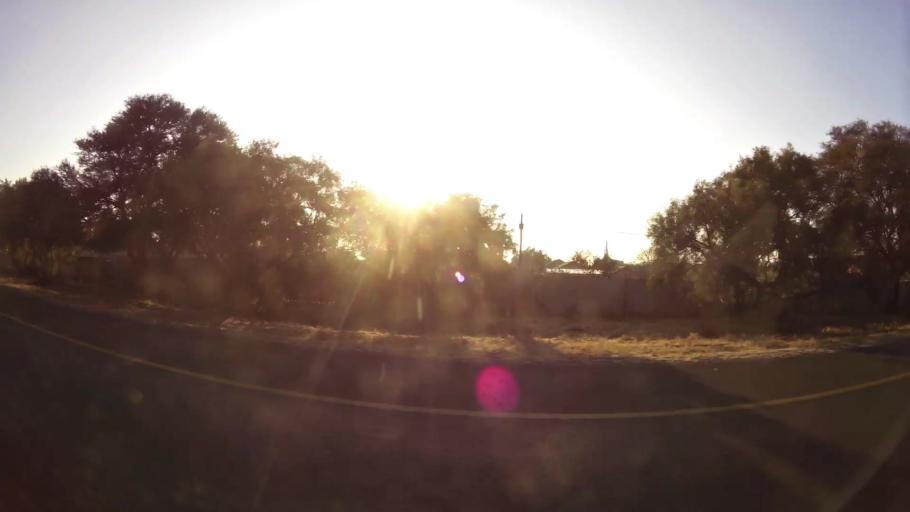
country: ZA
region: Orange Free State
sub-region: Mangaung Metropolitan Municipality
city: Bloemfontein
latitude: -29.1519
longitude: 26.1742
